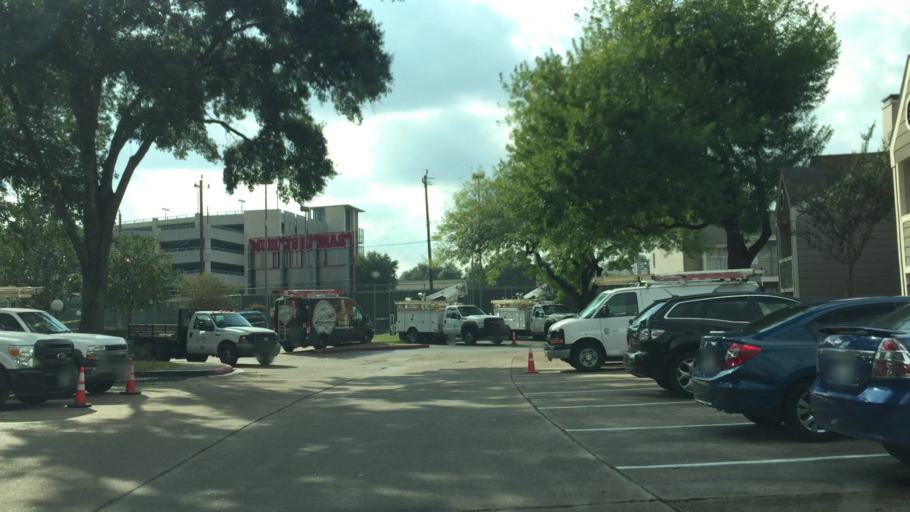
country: US
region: Texas
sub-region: Harris County
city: Houston
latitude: 29.7629
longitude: -95.4051
